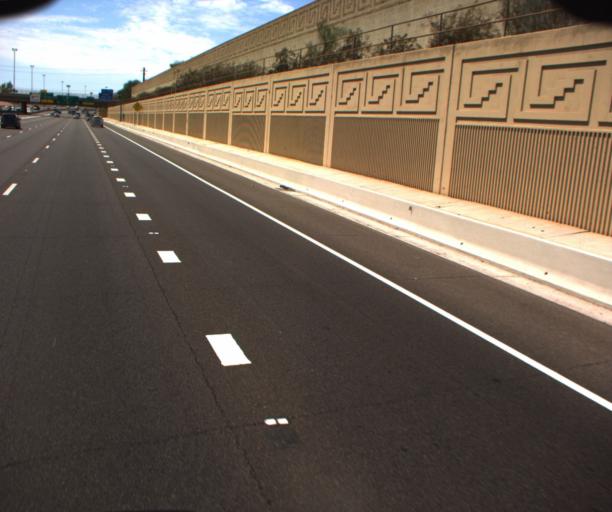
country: US
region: Arizona
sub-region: Maricopa County
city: Guadalupe
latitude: 33.3857
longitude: -111.9495
